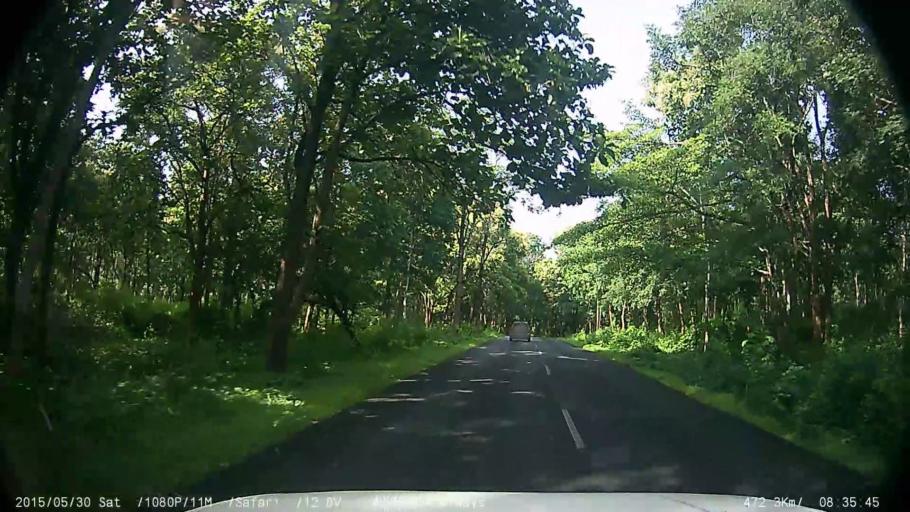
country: IN
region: Karnataka
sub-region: Mysore
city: Sargur
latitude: 11.7267
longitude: 76.4342
